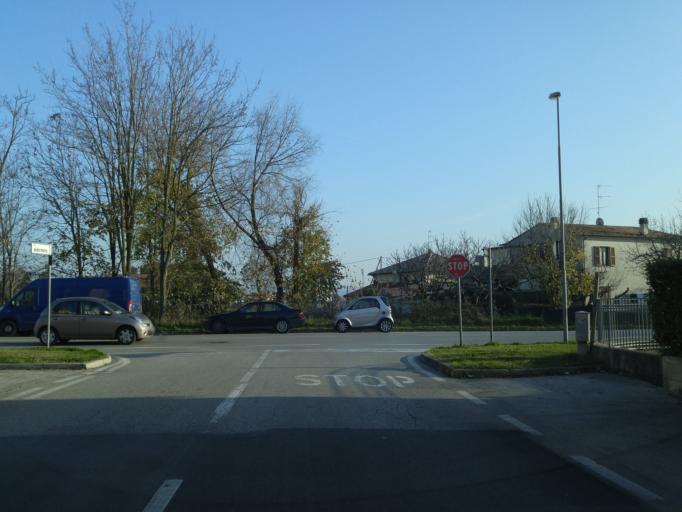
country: IT
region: The Marches
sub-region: Provincia di Pesaro e Urbino
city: Lucrezia
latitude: 43.7737
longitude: 12.9401
